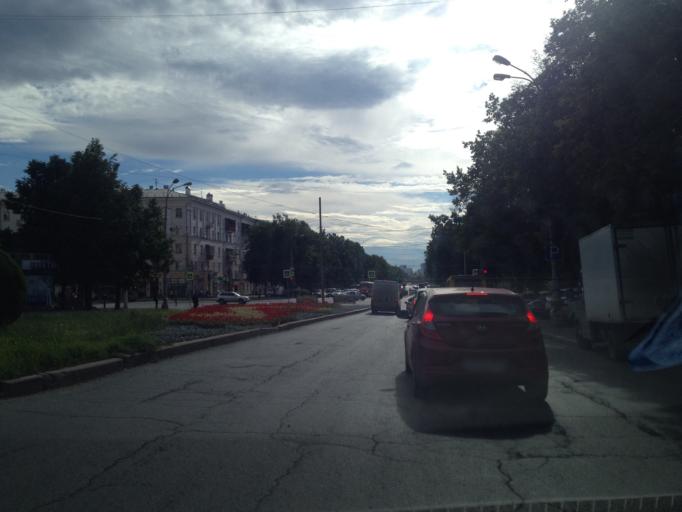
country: RU
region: Sverdlovsk
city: Yekaterinburg
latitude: 56.8437
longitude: 60.6472
